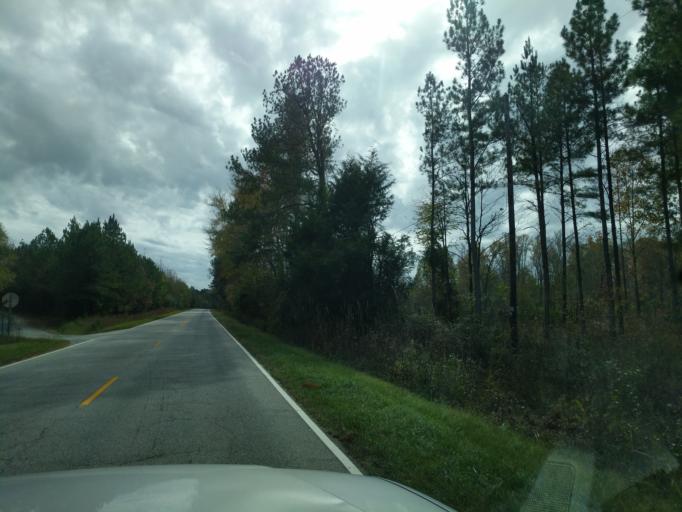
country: US
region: South Carolina
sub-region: Saluda County
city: Saluda
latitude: 34.1563
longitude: -81.8510
